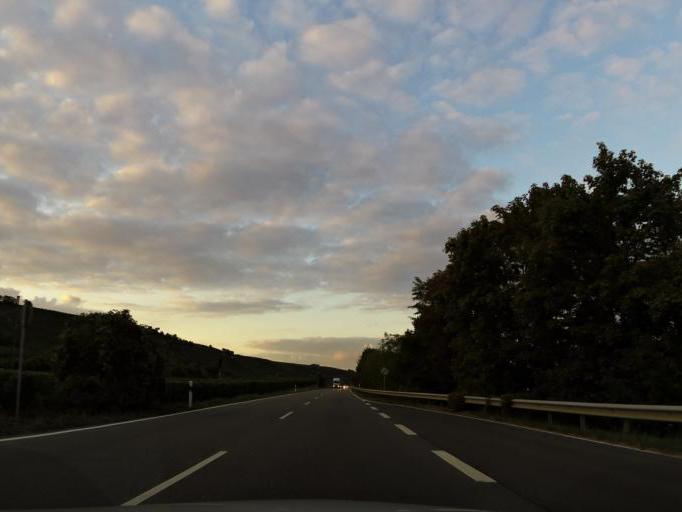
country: DE
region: Rheinland-Pfalz
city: Nierstein
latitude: 49.8871
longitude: 8.3383
